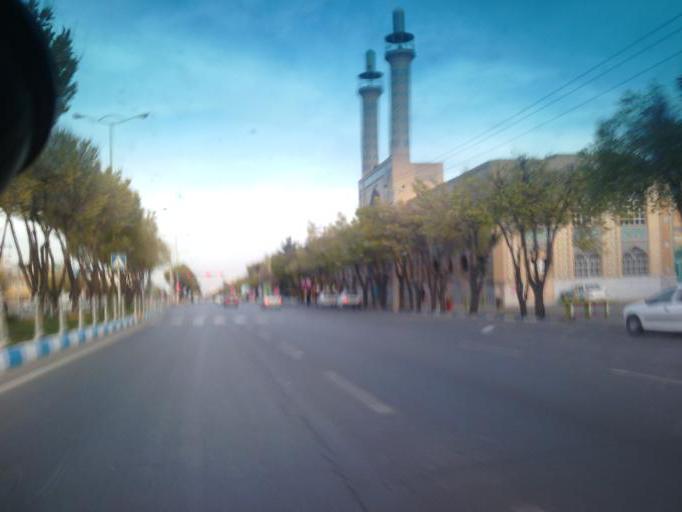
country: IR
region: Isfahan
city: Shahin Shahr
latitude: 32.8613
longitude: 51.5390
